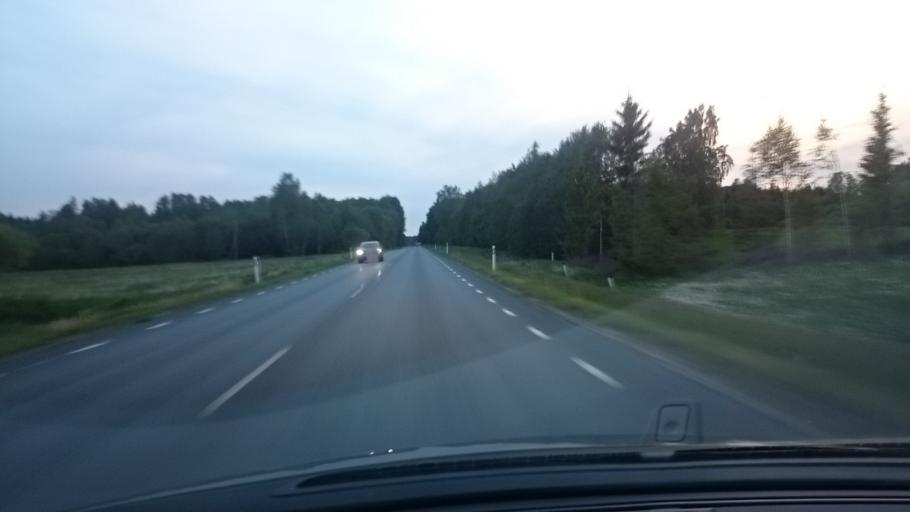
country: EE
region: Raplamaa
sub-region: Kehtna vald
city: Kehtna
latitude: 58.8504
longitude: 25.0261
